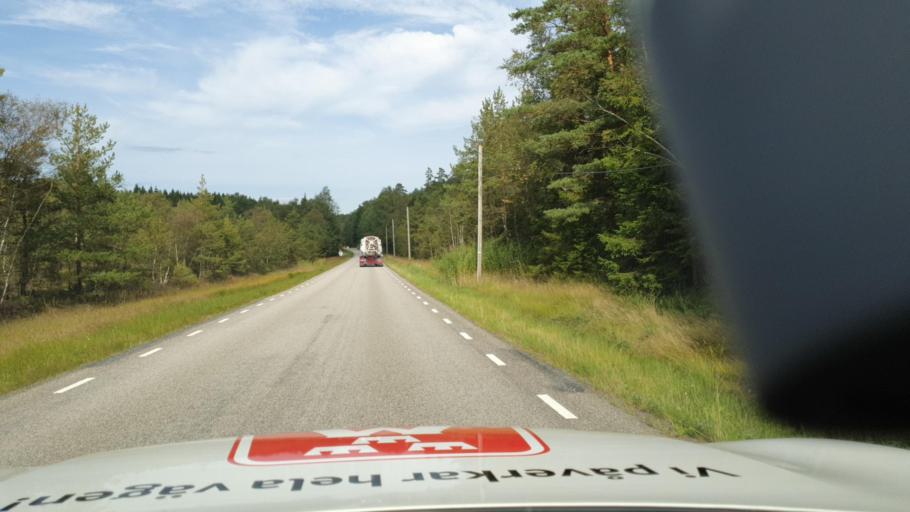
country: SE
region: Vaestra Goetaland
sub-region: Marks Kommun
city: Kinna
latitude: 57.4134
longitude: 12.6819
